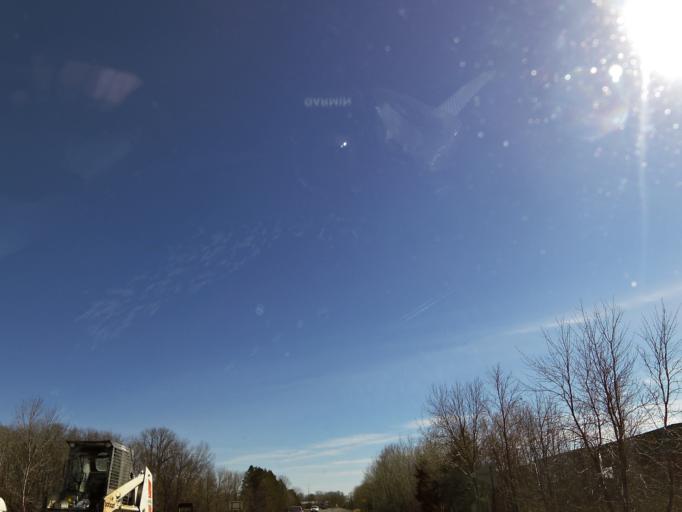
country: US
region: Minnesota
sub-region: Wright County
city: Buffalo
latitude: 45.1204
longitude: -93.8131
